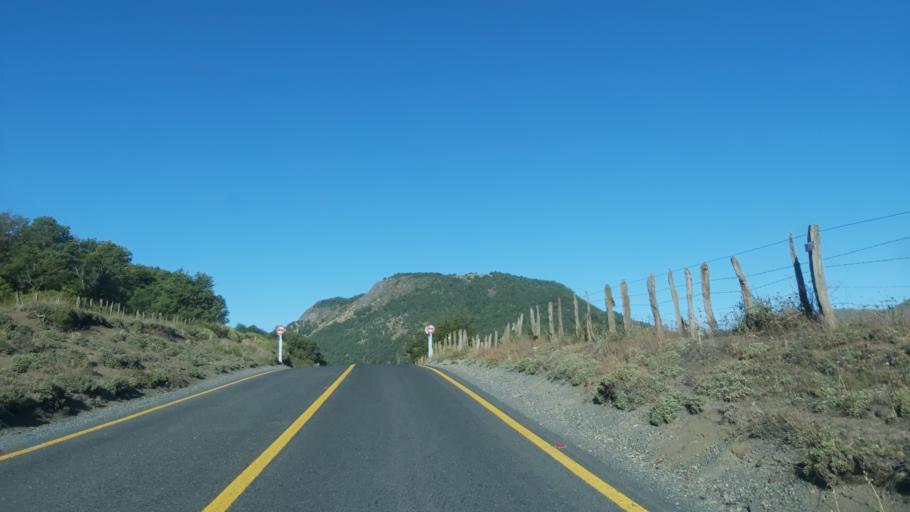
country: AR
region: Neuquen
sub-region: Departamento de Loncopue
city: Loncopue
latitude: -38.4447
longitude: -71.3474
